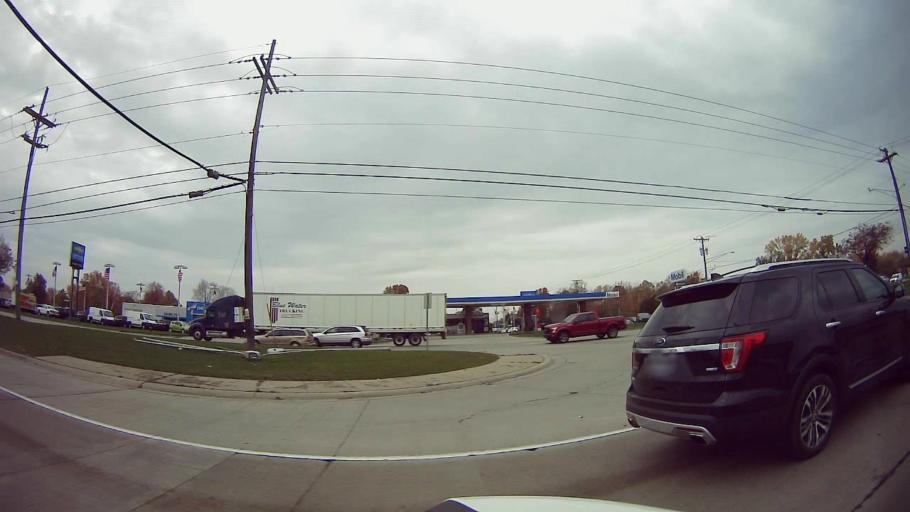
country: US
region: Michigan
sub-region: Macomb County
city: Sterling Heights
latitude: 42.5356
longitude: -83.0478
